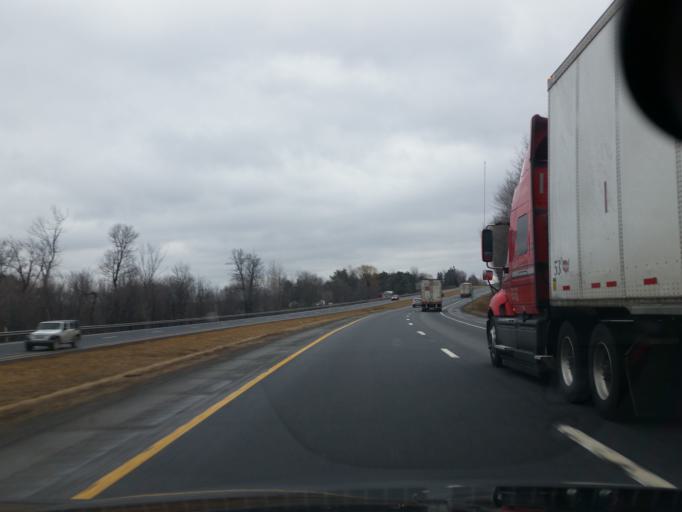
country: US
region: Pennsylvania
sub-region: Lackawanna County
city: Dalton
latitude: 41.6295
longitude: -75.6438
